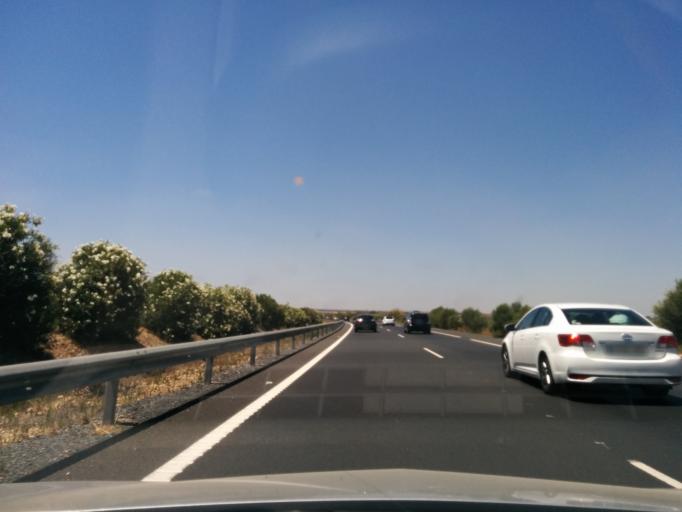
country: ES
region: Andalusia
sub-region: Provincia de Huelva
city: Bonares
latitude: 37.3427
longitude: -6.6811
